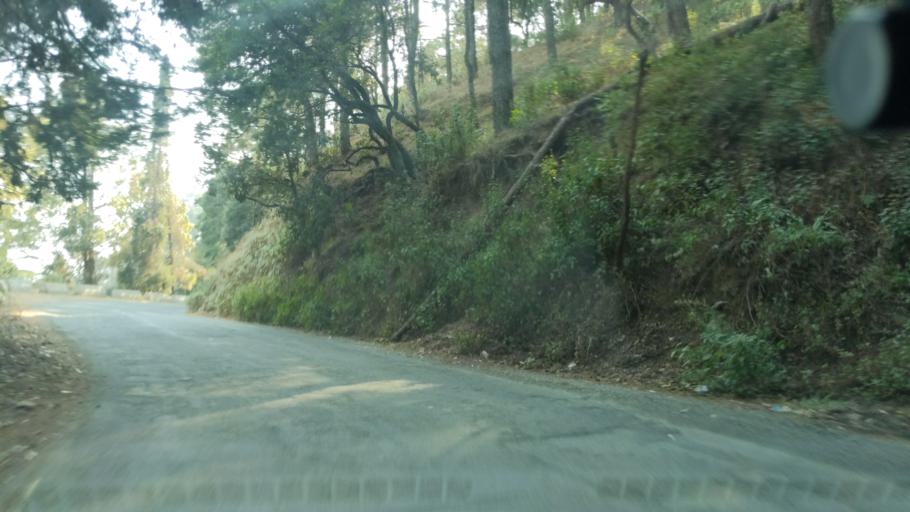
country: IN
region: Uttarakhand
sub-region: Naini Tal
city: Bhowali
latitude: 29.3977
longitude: 79.5379
